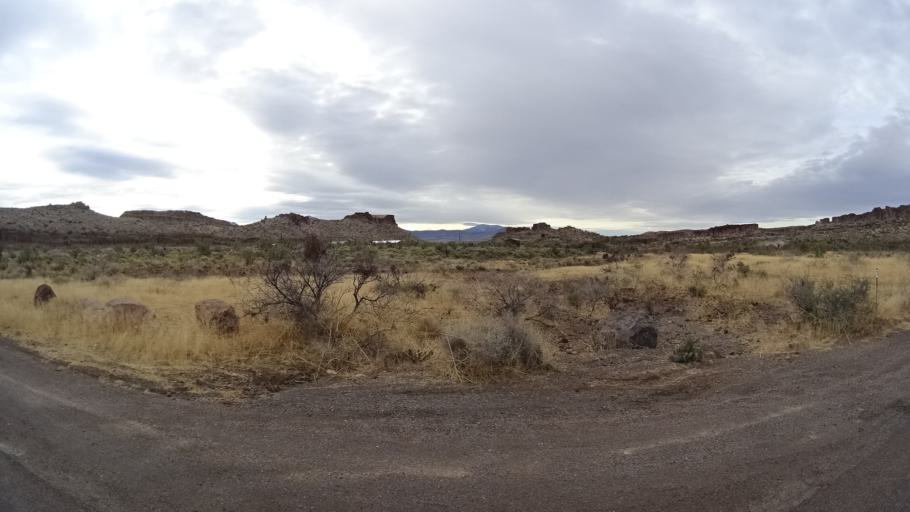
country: US
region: Arizona
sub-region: Mohave County
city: Kingman
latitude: 35.2172
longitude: -114.0724
